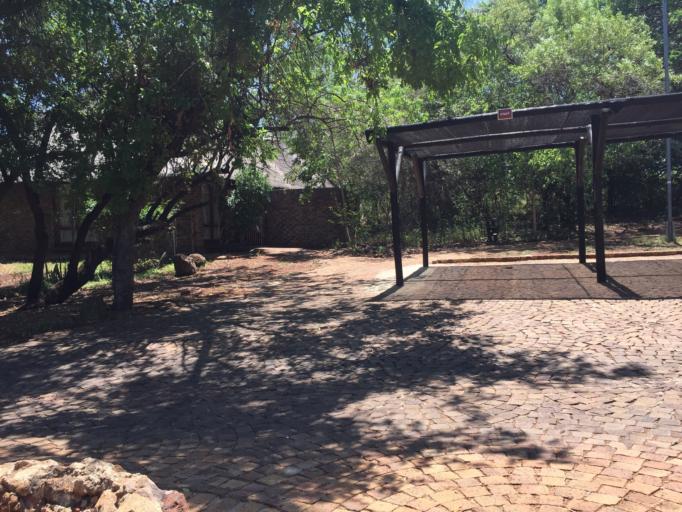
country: ZA
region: North-West
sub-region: Bojanala Platinum District Municipality
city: Mogwase
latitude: -25.3434
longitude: 27.0574
